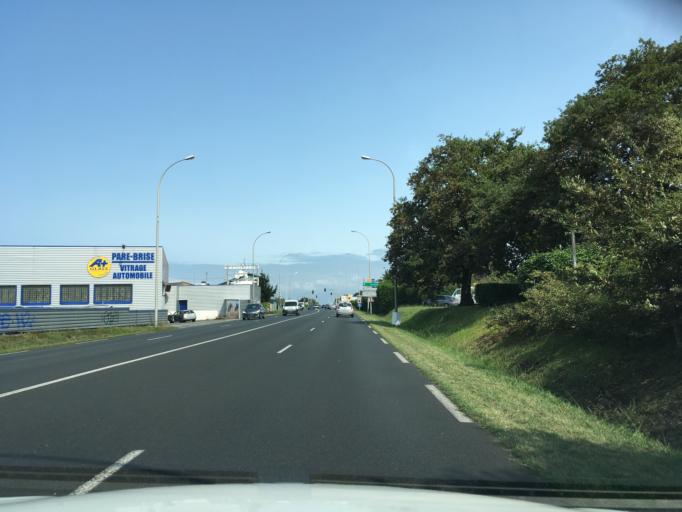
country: FR
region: Aquitaine
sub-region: Departement des Pyrenees-Atlantiques
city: Biarritz
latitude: 43.4854
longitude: -1.5381
